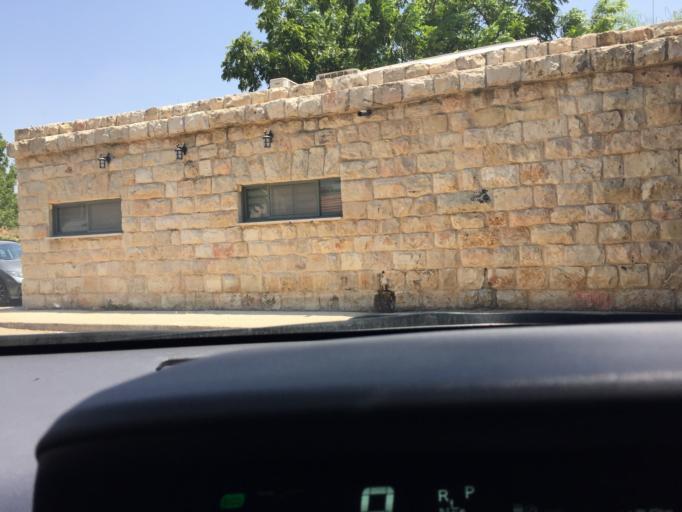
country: IL
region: Central District
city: Yehud
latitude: 32.0431
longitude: 34.9034
